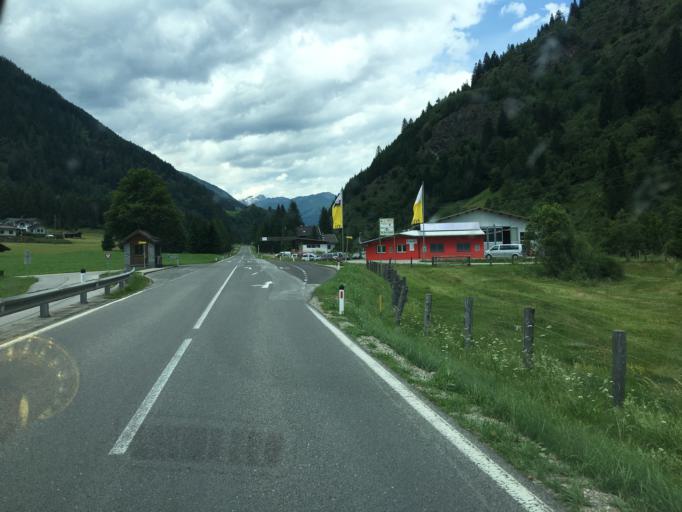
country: AT
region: Carinthia
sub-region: Politischer Bezirk Spittal an der Drau
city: Mortschach
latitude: 46.9352
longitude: 12.9033
